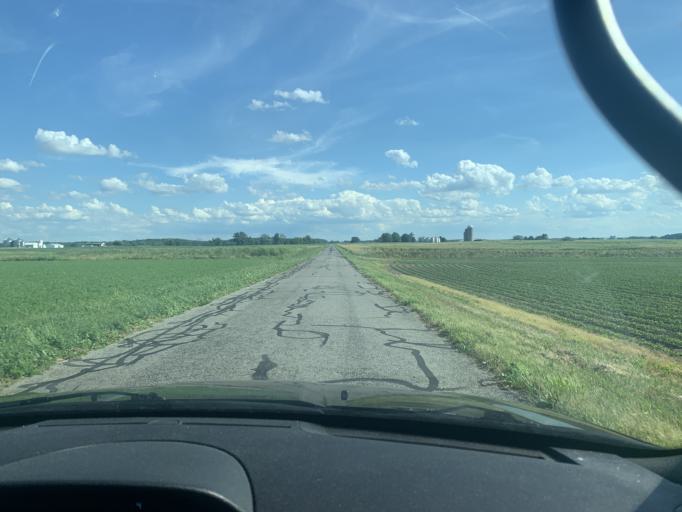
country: US
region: Ohio
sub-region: Logan County
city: De Graff
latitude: 40.3322
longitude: -83.8724
